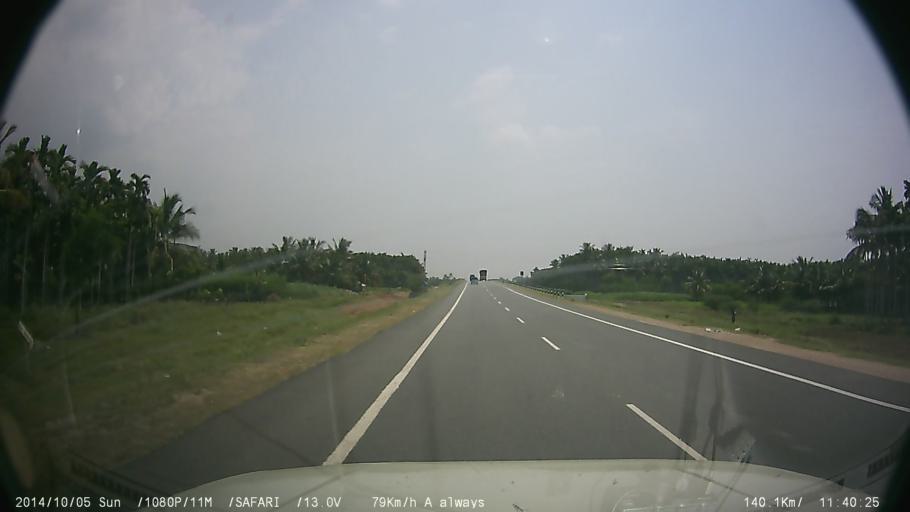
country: IN
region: Tamil Nadu
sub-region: Salem
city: Attur
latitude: 11.6118
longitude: 78.5874
